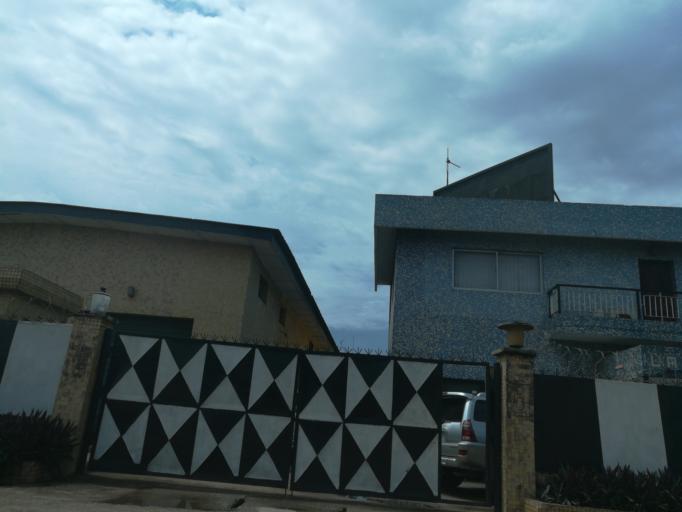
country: NG
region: Lagos
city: Agege
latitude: 6.6078
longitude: 3.3292
